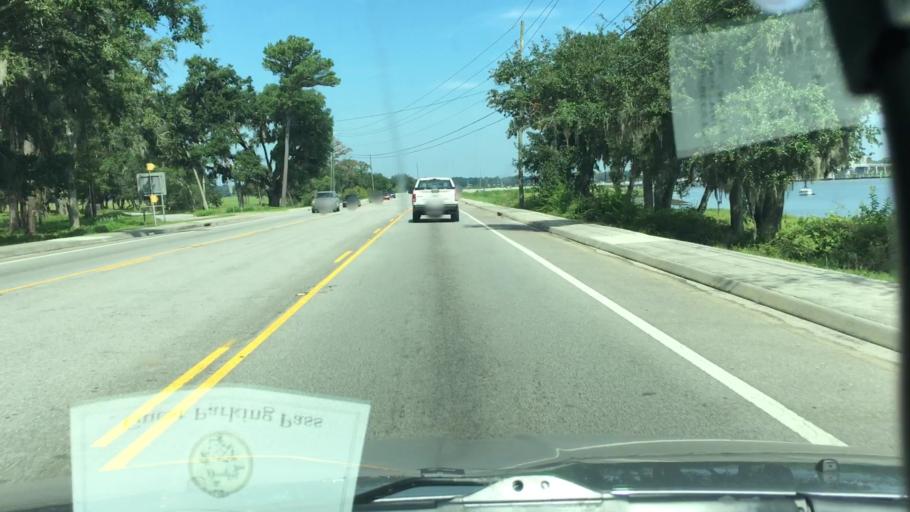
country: US
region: South Carolina
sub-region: Beaufort County
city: Beaufort
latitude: 32.4206
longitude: -80.6637
